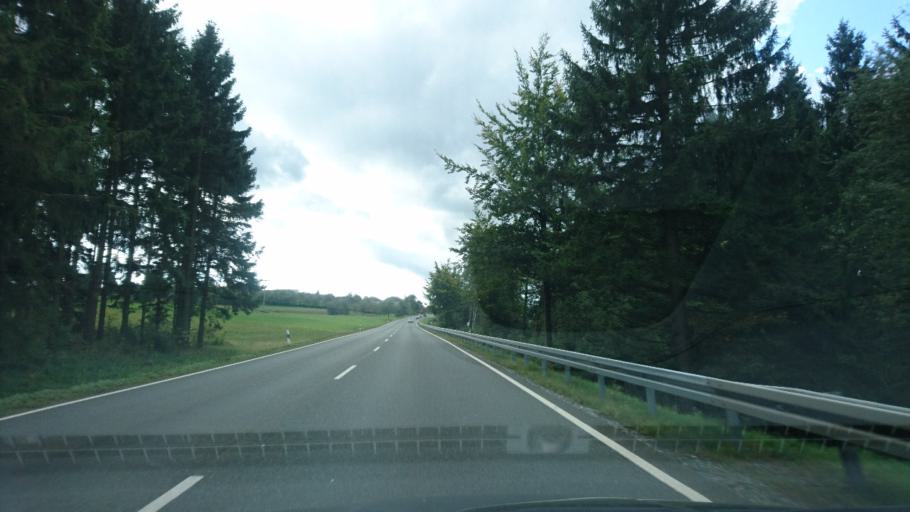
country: DE
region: Bavaria
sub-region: Upper Franconia
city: Geroldsgrun
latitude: 50.2952
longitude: 11.6389
